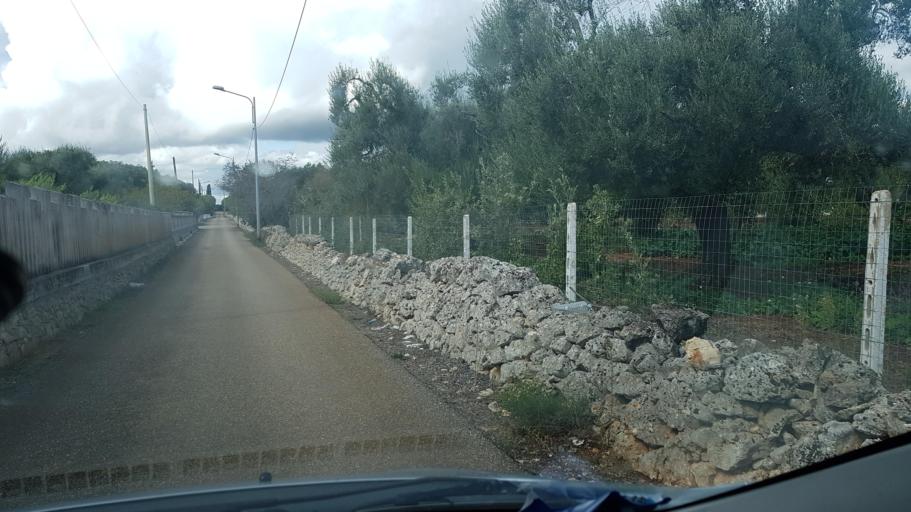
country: IT
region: Apulia
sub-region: Provincia di Brindisi
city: San Vito dei Normanni
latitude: 40.6537
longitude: 17.7341
